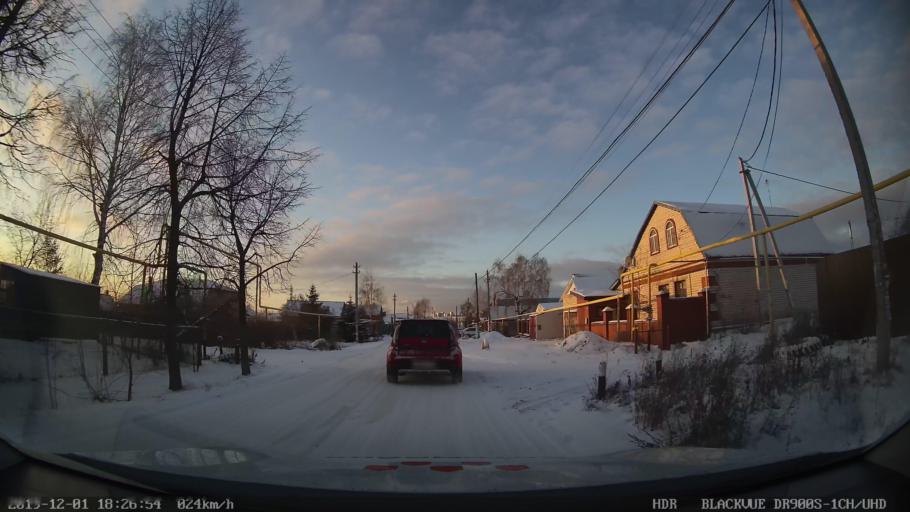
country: RU
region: Tatarstan
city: Vysokaya Gora
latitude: 55.8061
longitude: 49.2554
